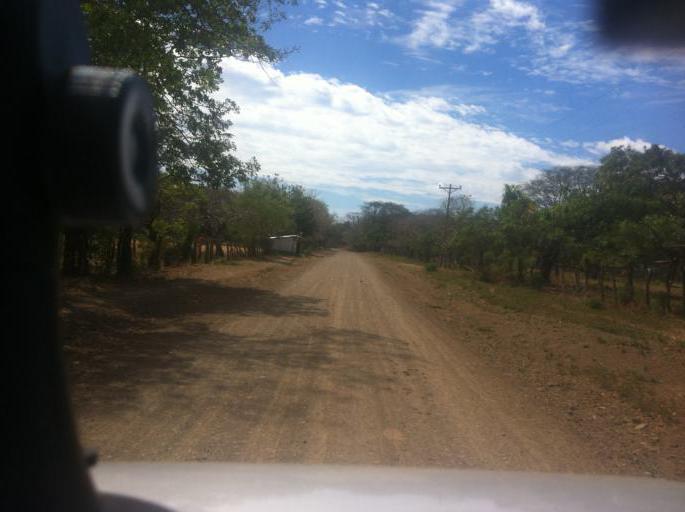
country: NI
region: Granada
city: Nandaime
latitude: 11.6201
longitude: -86.0260
